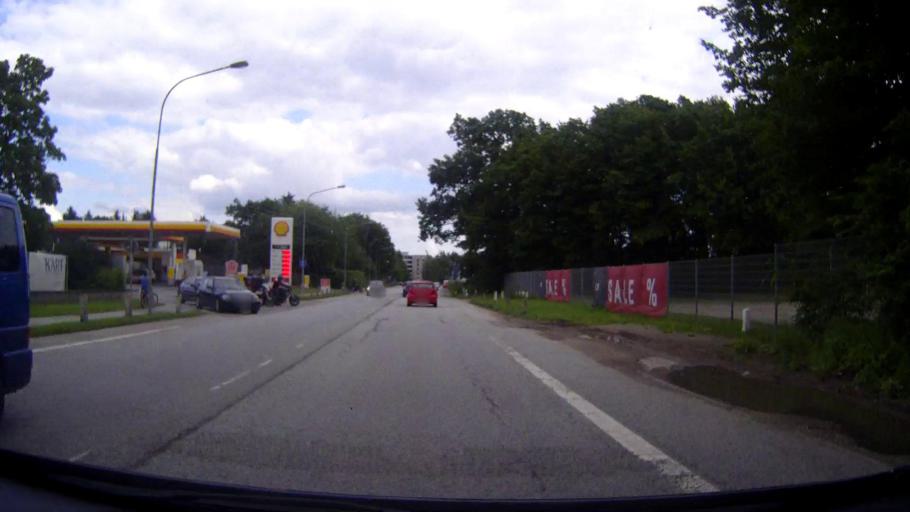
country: DE
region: Schleswig-Holstein
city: Stockelsdorf
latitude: 53.8561
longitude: 10.6354
